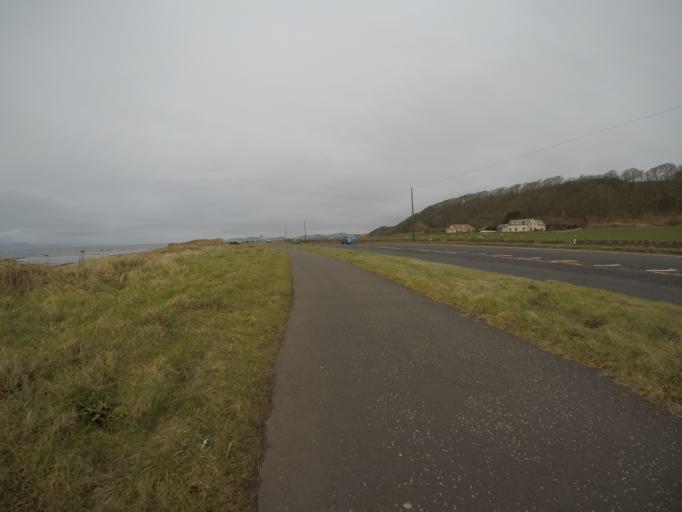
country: GB
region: Scotland
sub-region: North Ayrshire
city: West Kilbride
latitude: 55.6678
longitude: -4.8419
